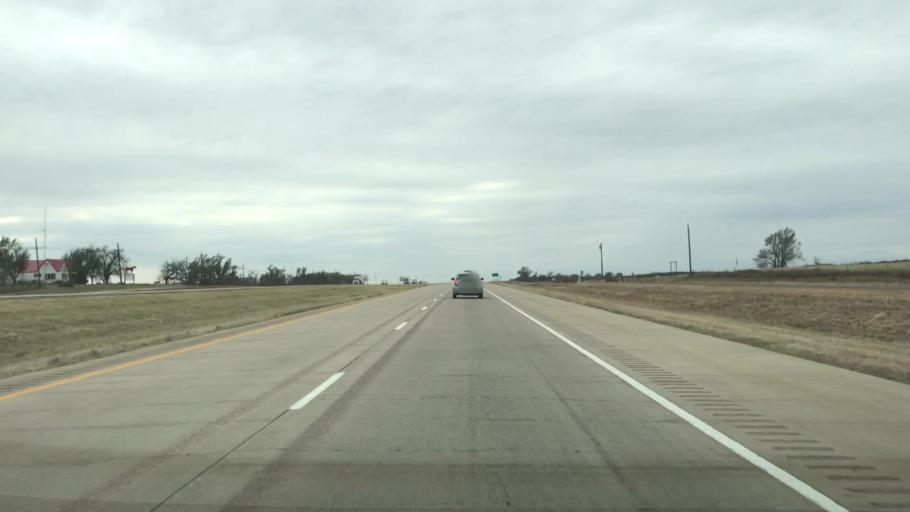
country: US
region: Texas
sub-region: Wheeler County
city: Shamrock
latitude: 35.2270
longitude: -100.1811
